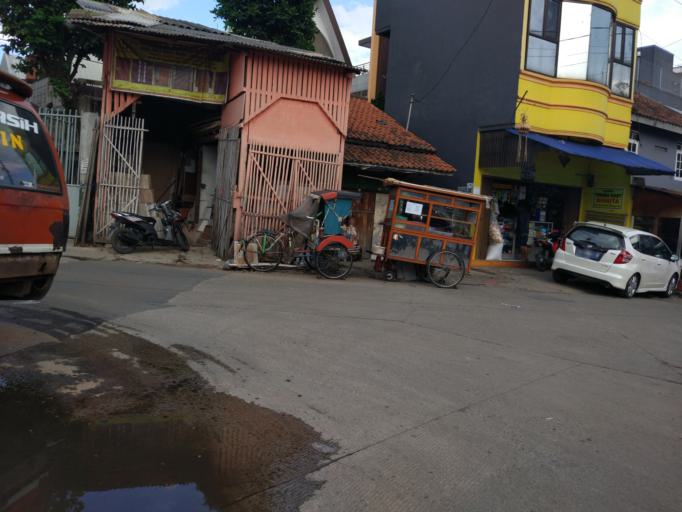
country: ID
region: West Java
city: Bandung
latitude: -6.9235
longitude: 107.5813
